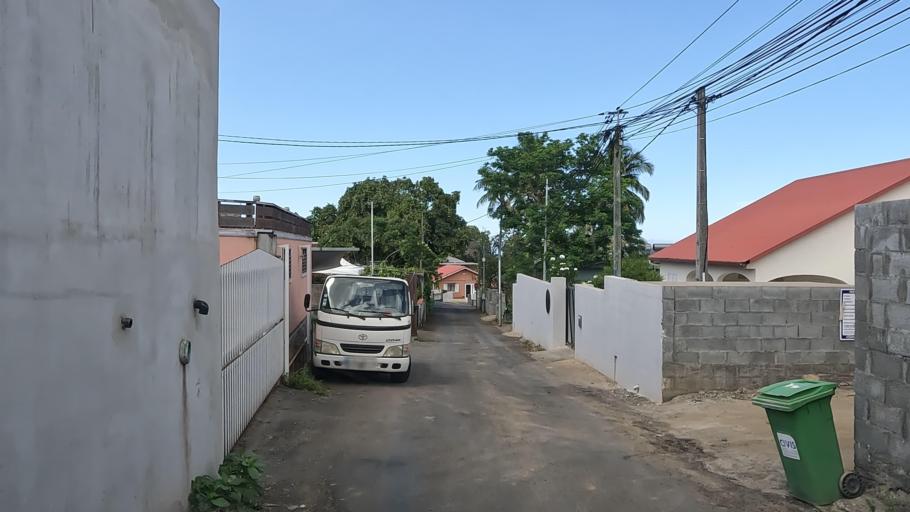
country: RE
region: Reunion
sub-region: Reunion
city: L'Entre-Deux
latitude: -21.2672
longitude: 55.4498
